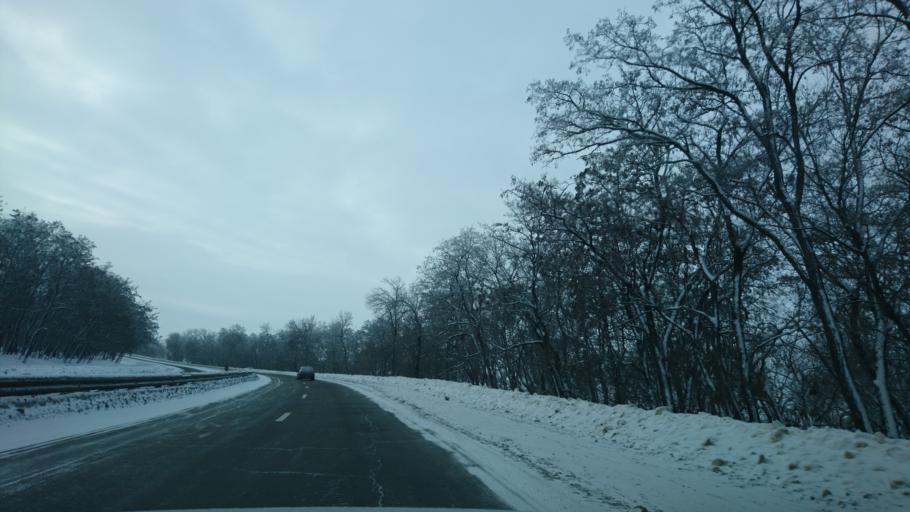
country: RU
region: Belgorod
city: Mayskiy
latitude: 50.4829
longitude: 36.4071
